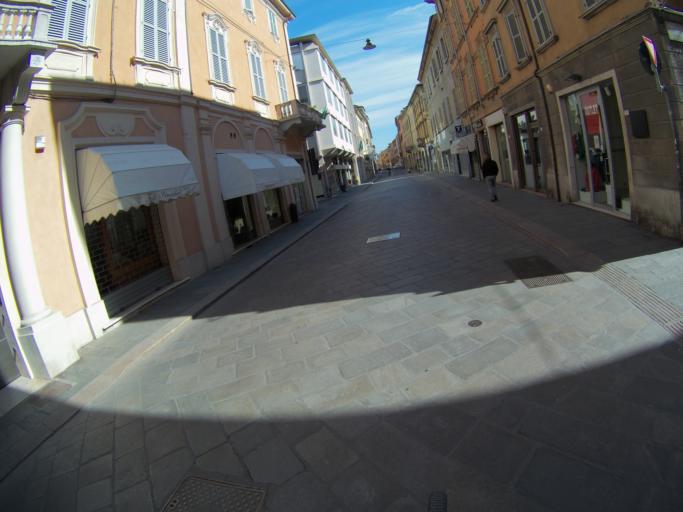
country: IT
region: Emilia-Romagna
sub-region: Provincia di Reggio Emilia
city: Reggio nell'Emilia
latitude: 44.6979
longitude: 10.6330
